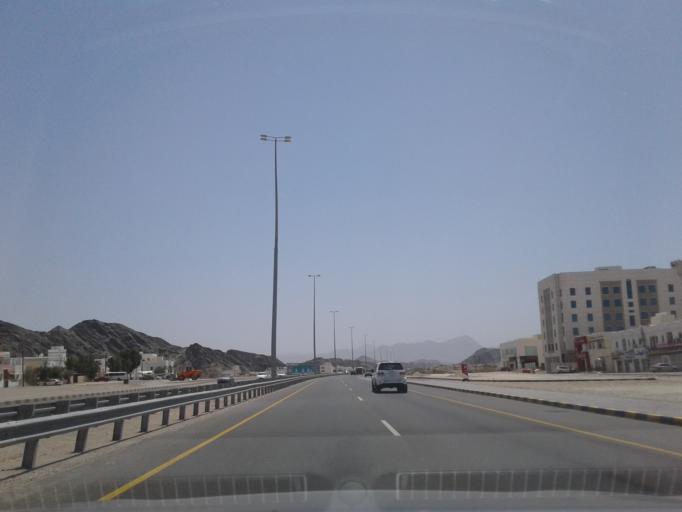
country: OM
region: Muhafazat Masqat
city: Bawshar
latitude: 23.4854
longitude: 58.4993
